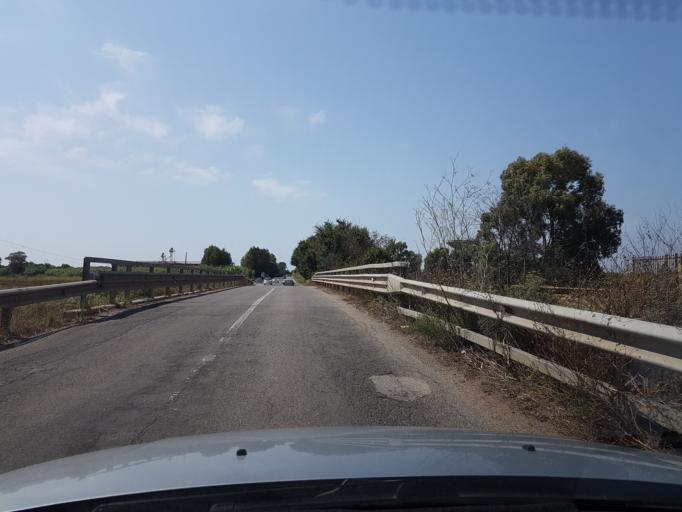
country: IT
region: Sardinia
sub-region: Provincia di Oristano
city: Solanas
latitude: 39.9201
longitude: 8.5487
